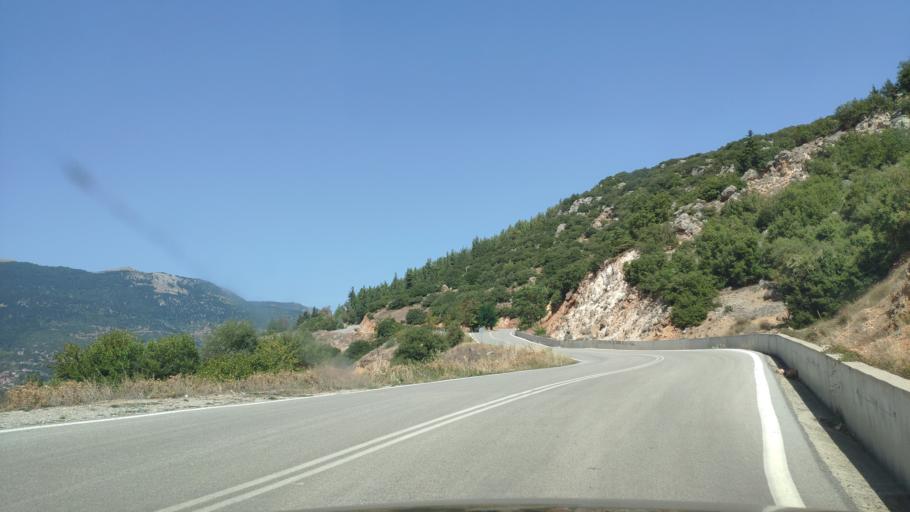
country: GR
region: West Greece
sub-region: Nomos Achaias
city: Aiyira
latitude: 37.9231
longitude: 22.3388
